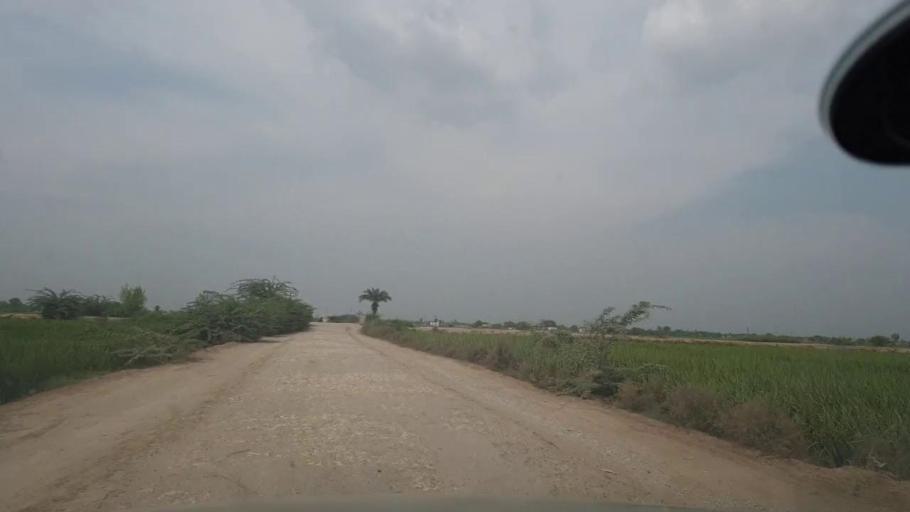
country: PK
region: Sindh
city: Jacobabad
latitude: 28.2517
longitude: 68.4368
